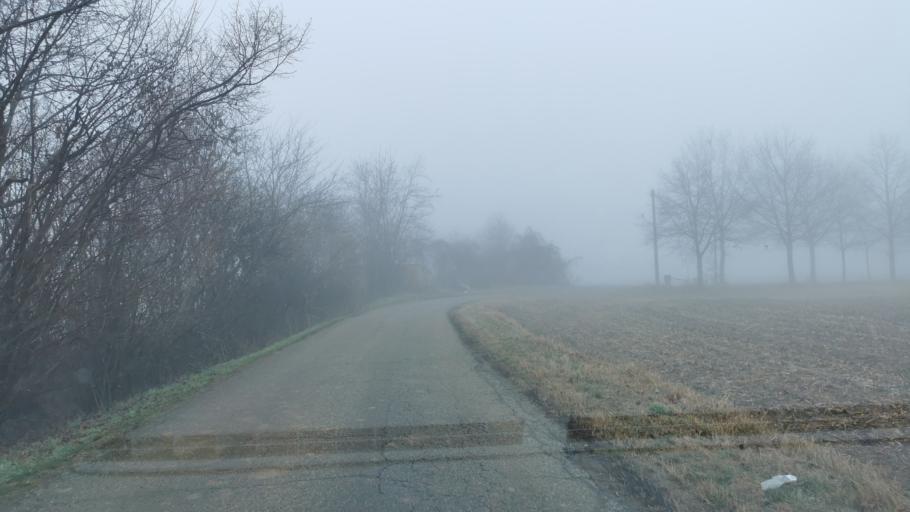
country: IT
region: Piedmont
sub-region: Provincia di Torino
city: Leini
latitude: 45.1903
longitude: 7.7350
